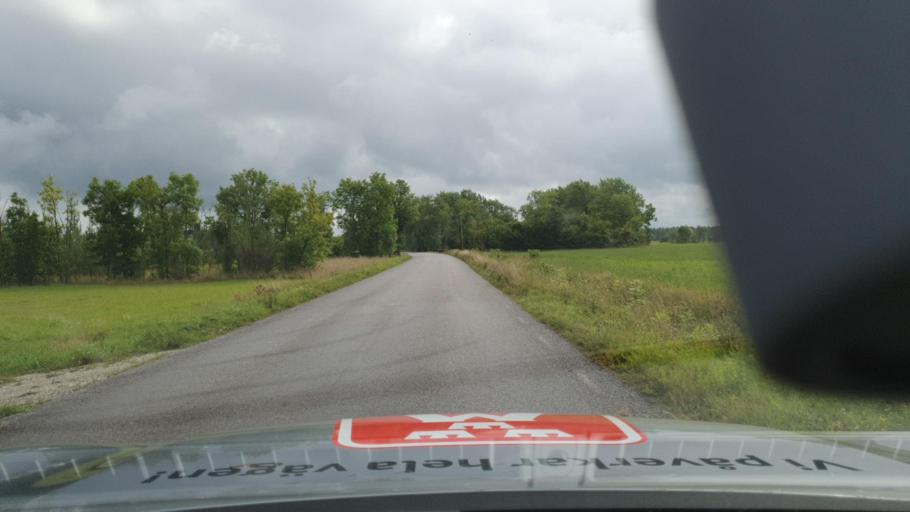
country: SE
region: Gotland
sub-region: Gotland
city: Slite
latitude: 57.6959
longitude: 18.7598
